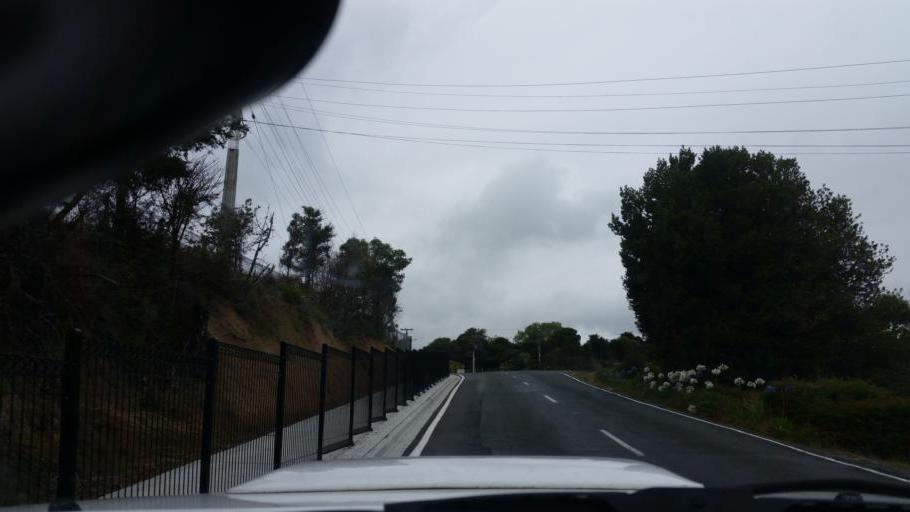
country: NZ
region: Auckland
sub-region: Auckland
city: Wellsford
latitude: -36.1603
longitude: 174.4466
